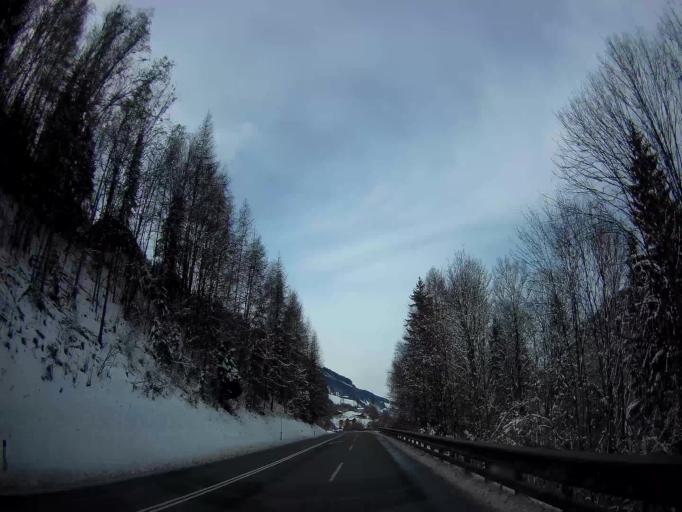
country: AT
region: Salzburg
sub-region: Politischer Bezirk Sankt Johann im Pongau
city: Goldegg
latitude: 47.2994
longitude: 13.0928
